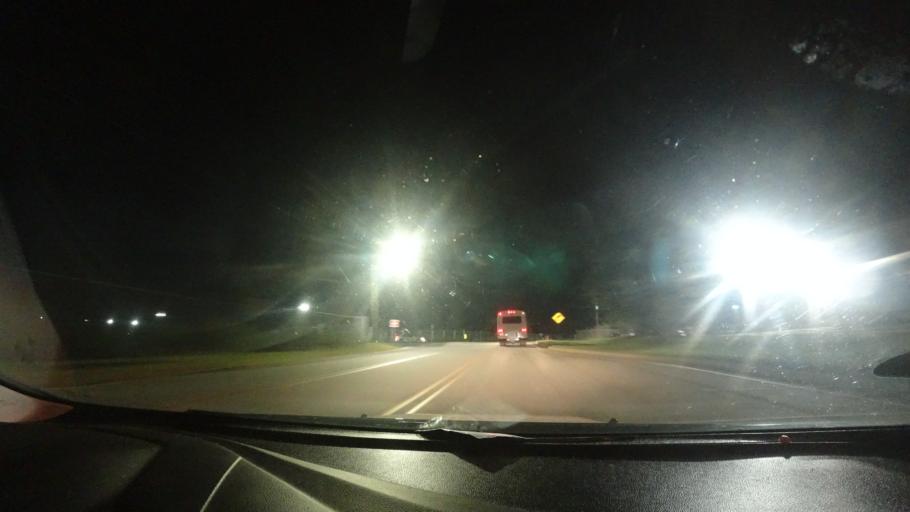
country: US
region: Georgia
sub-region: Fulton County
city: College Park
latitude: 33.6272
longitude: -84.4391
